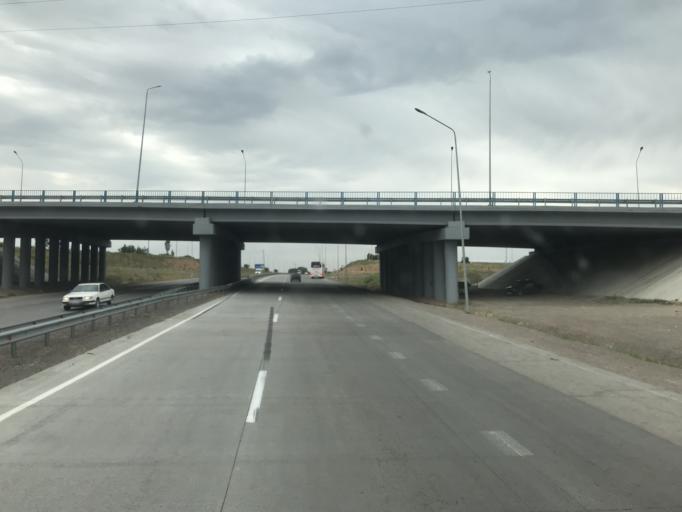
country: UZ
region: Toshkent
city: Salor
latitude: 41.5003
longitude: 69.3562
